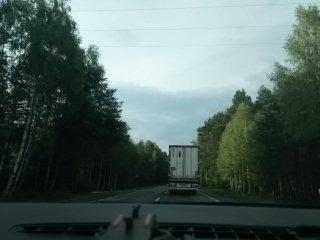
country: PL
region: Subcarpathian Voivodeship
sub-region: Powiat nizanski
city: Jarocin
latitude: 50.6310
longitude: 22.2865
